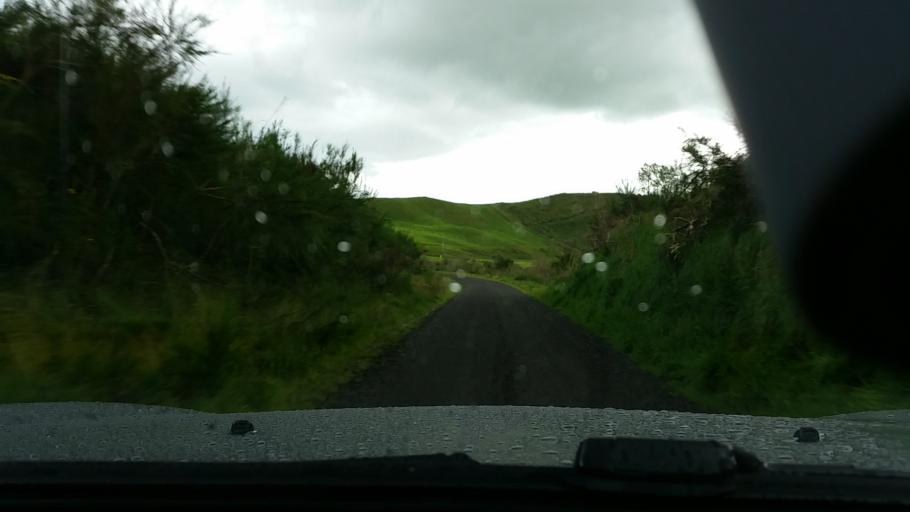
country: NZ
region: Waikato
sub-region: Taupo District
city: Taupo
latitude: -38.4969
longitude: 176.2044
